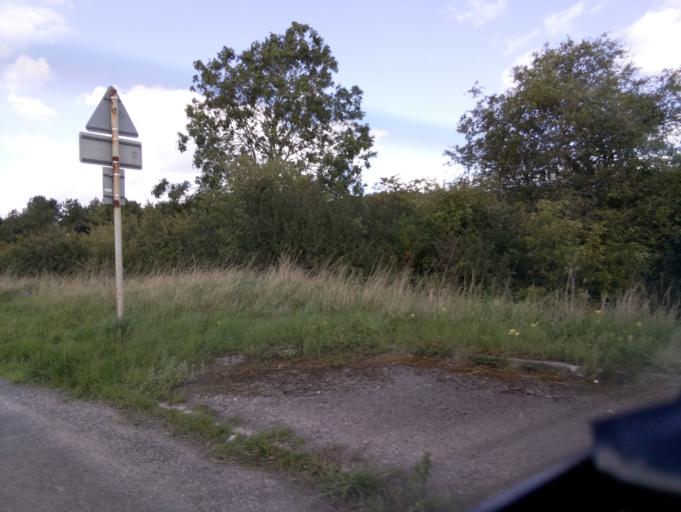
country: GB
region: England
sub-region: Wiltshire
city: Stockton
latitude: 51.2018
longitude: -2.0080
